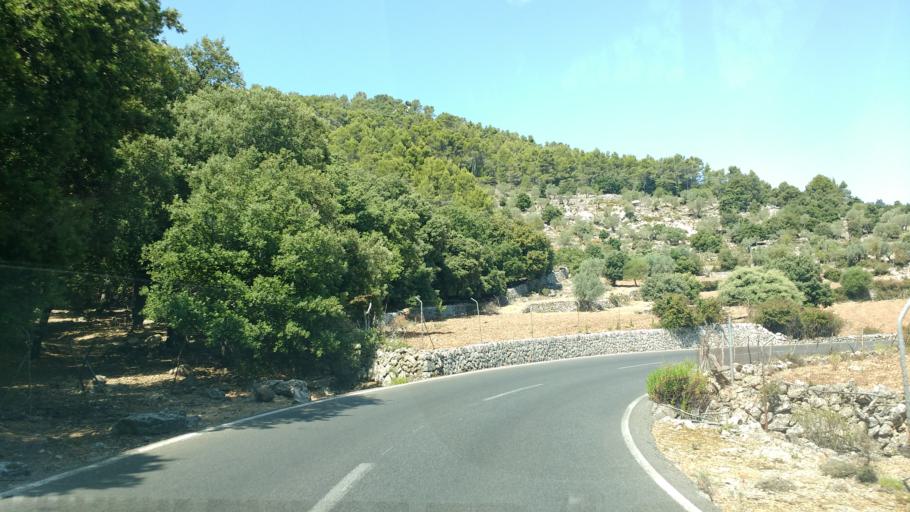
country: ES
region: Balearic Islands
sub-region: Illes Balears
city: Escorca
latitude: 39.8259
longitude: 2.8396
